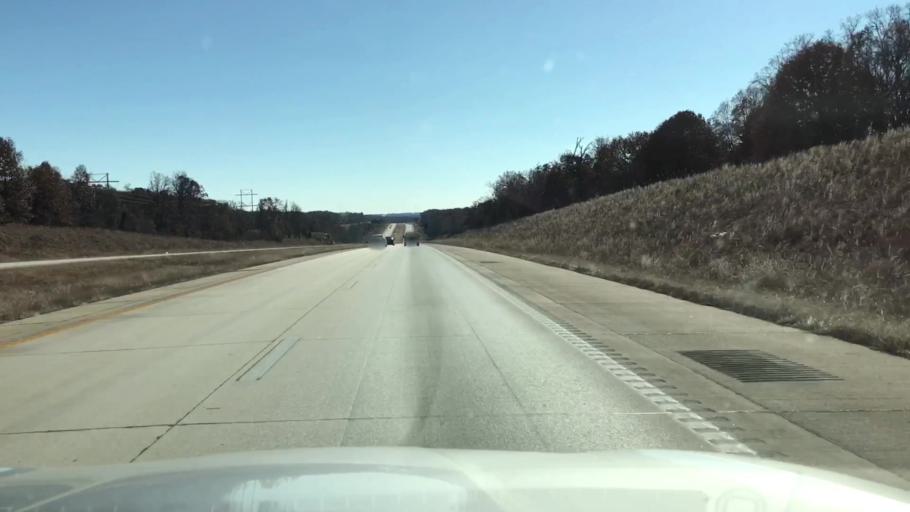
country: US
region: Missouri
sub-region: Jasper County
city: Duquesne
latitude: 37.0233
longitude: -94.4302
